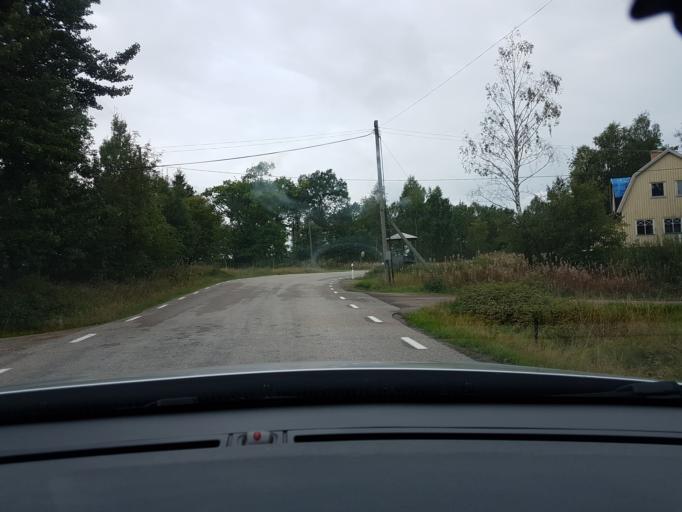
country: SE
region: Vaestra Goetaland
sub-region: Ale Kommun
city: Alvangen
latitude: 57.9133
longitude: 12.1451
